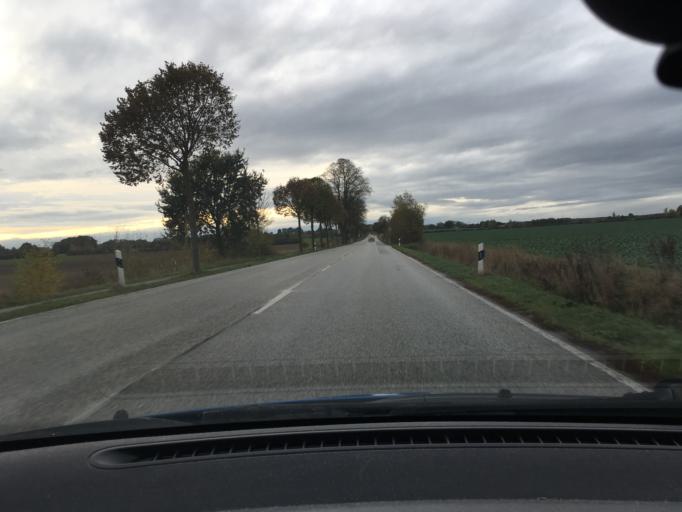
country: DE
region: Schleswig-Holstein
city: Dassendorf
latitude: 53.4890
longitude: 10.4011
